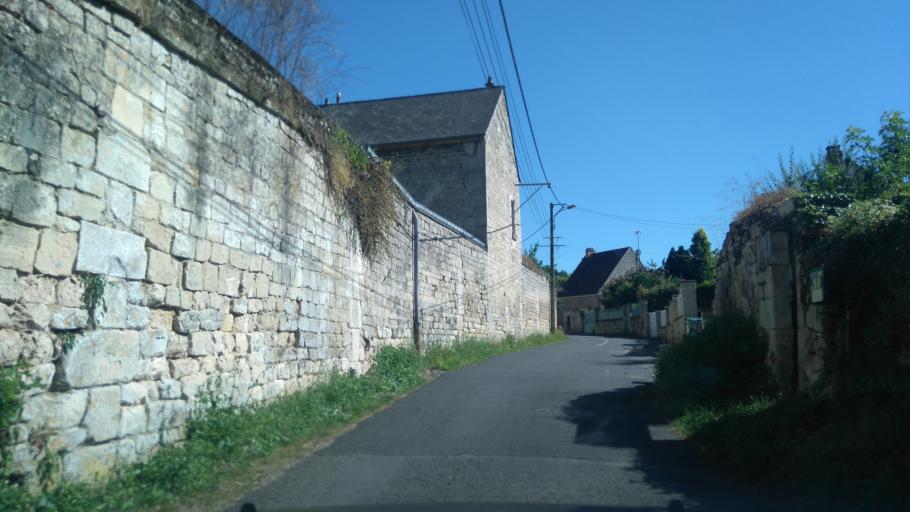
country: FR
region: Picardie
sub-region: Departement de l'Oise
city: Saint-Maximin
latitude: 49.2232
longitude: 2.4499
